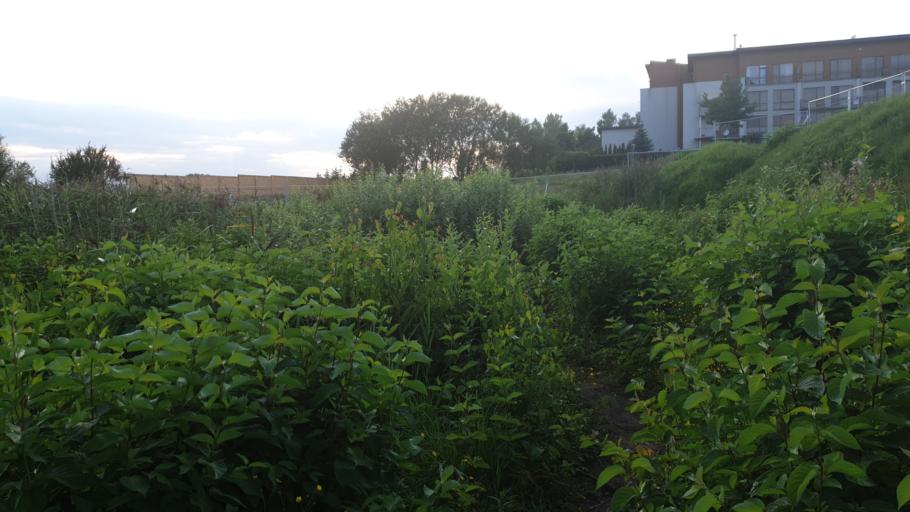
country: LT
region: Vilnius County
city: Pilaite
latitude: 54.7050
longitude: 25.1612
